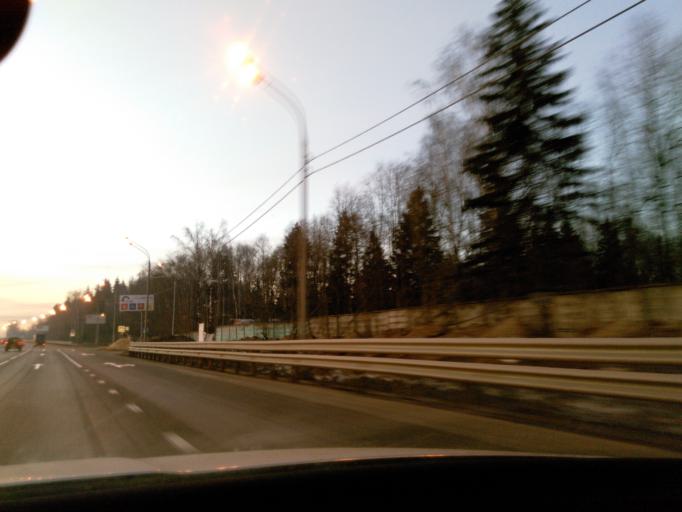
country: RU
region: Moskovskaya
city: Rzhavki
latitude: 55.9910
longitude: 37.2666
